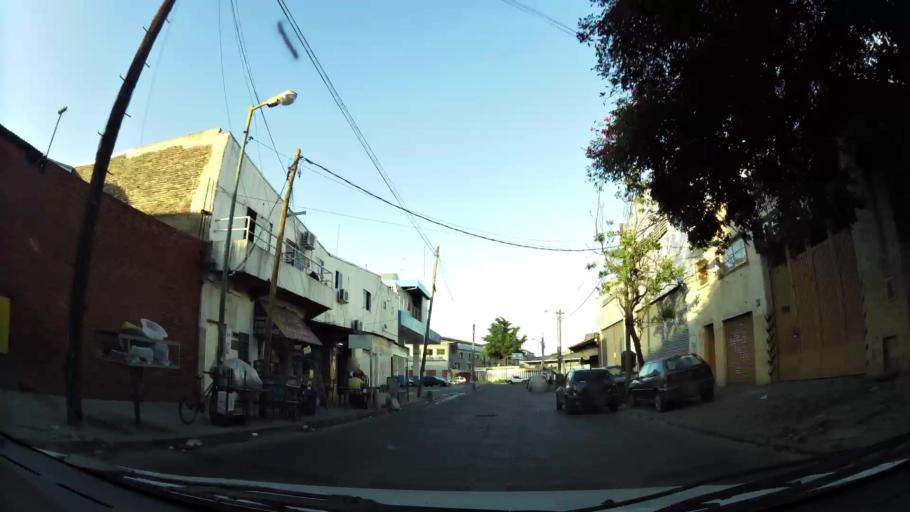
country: AR
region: Buenos Aires
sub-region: Partido de General San Martin
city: General San Martin
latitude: -34.5559
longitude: -58.5217
